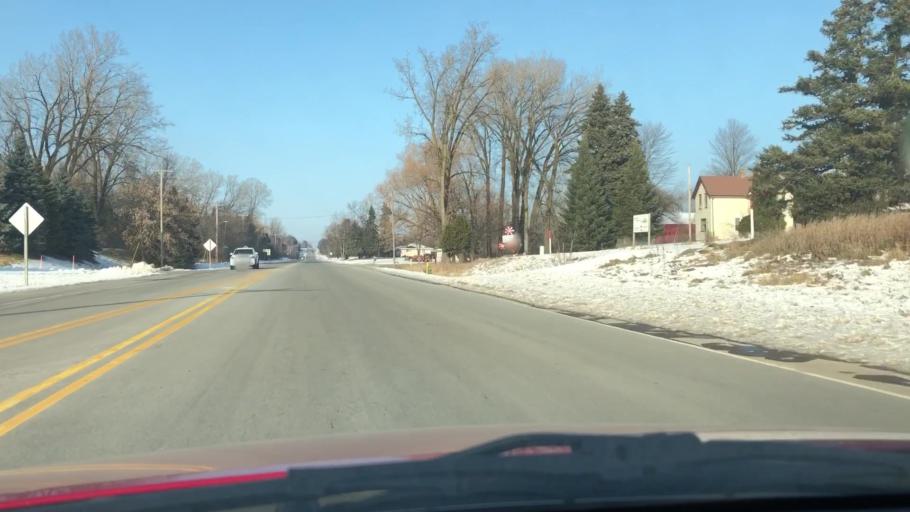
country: US
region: Wisconsin
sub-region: Outagamie County
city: Kimberly
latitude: 44.3181
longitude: -88.3749
